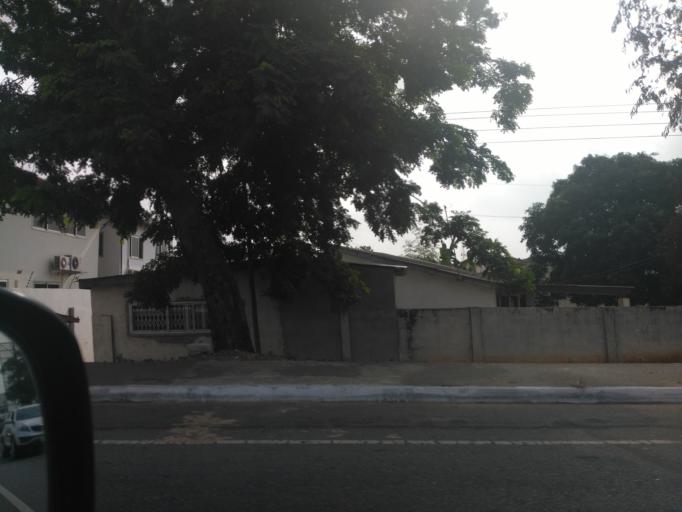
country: GH
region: Greater Accra
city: Accra
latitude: 5.5791
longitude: -0.1959
